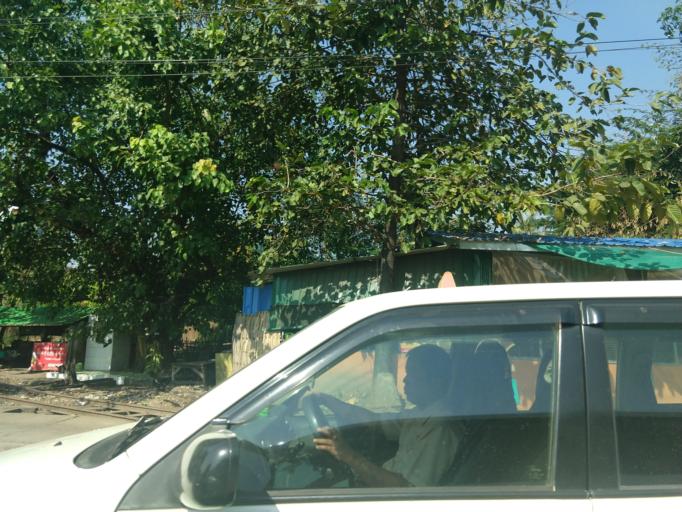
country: MM
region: Yangon
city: Yangon
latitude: 16.7695
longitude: 96.1717
